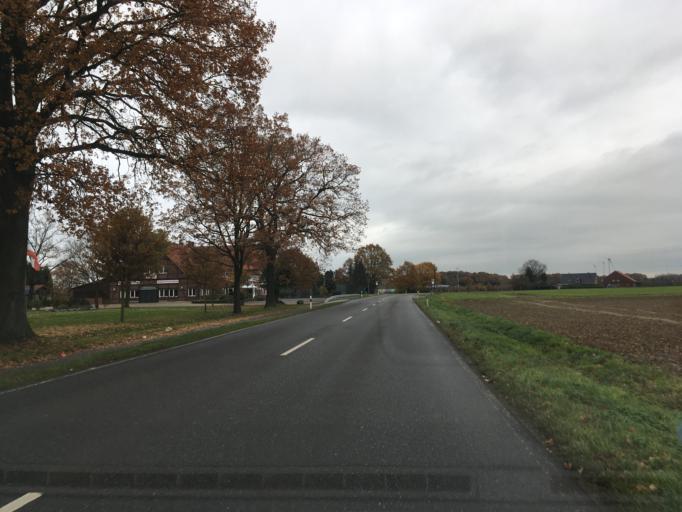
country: DE
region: North Rhine-Westphalia
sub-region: Regierungsbezirk Munster
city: Gescher
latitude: 51.9715
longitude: 7.0147
